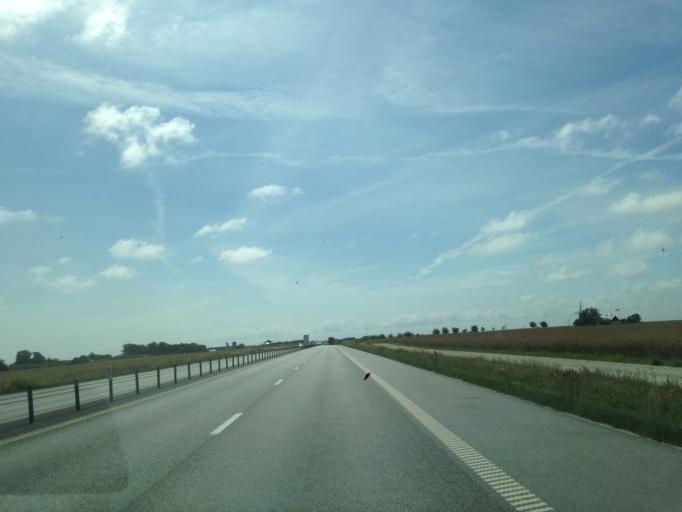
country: SE
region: Skane
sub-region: Trelleborgs Kommun
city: Skare
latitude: 55.4154
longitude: 13.0633
